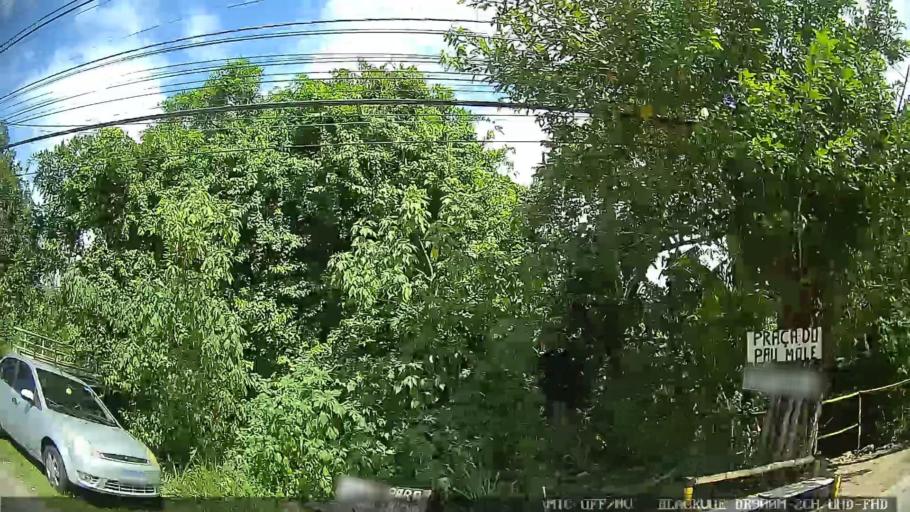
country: BR
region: Sao Paulo
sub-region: Peruibe
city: Peruibe
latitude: -24.3074
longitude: -47.0125
